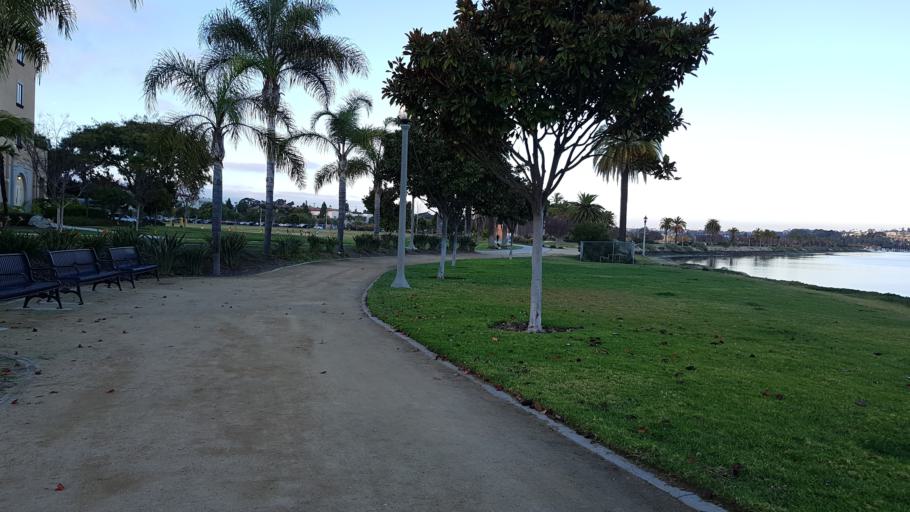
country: US
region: California
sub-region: San Diego County
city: Coronado
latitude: 32.7305
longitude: -117.2151
